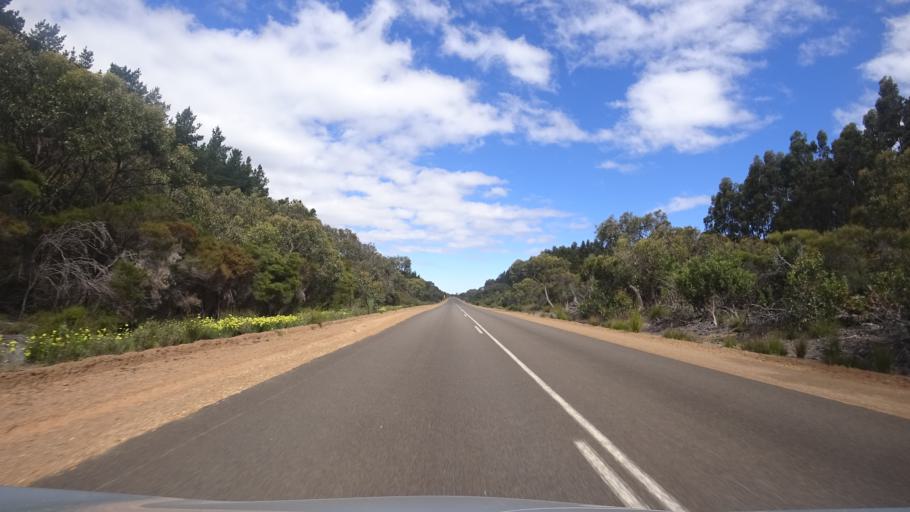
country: AU
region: South Australia
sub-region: Kangaroo Island
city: Kingscote
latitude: -35.7923
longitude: 137.0179
